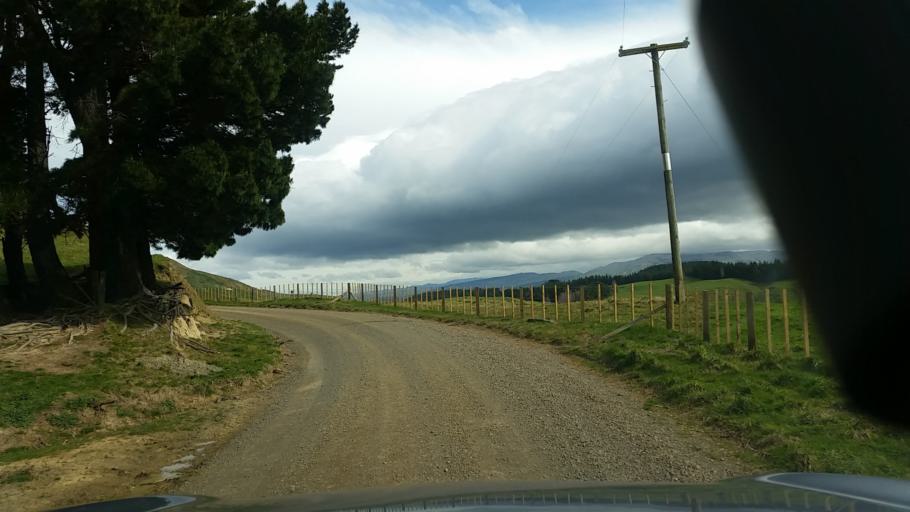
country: NZ
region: Hawke's Bay
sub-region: Napier City
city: Napier
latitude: -39.2044
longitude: 176.9403
